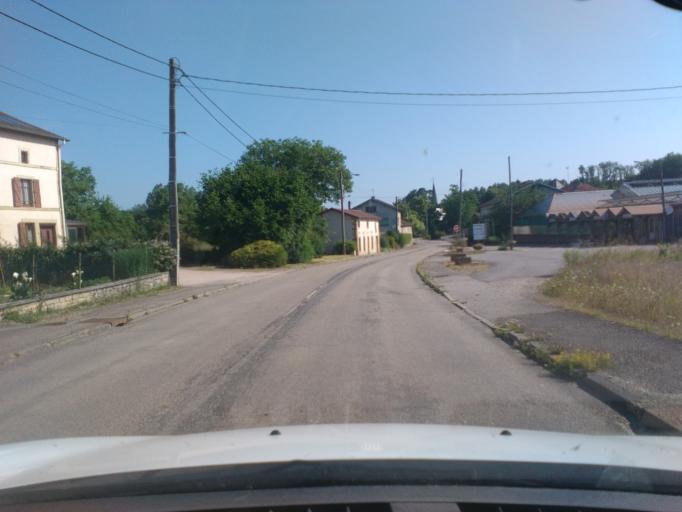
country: FR
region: Lorraine
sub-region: Departement des Vosges
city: Aydoilles
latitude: 48.2440
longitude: 6.6006
